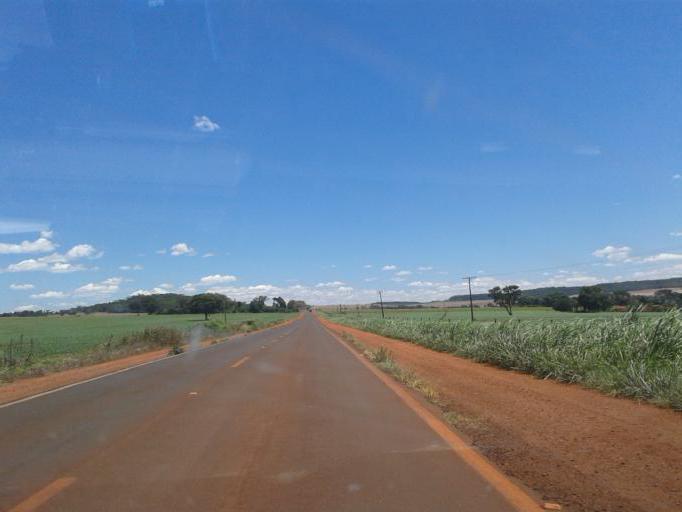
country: BR
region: Minas Gerais
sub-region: Capinopolis
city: Capinopolis
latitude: -18.5981
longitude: -49.5207
